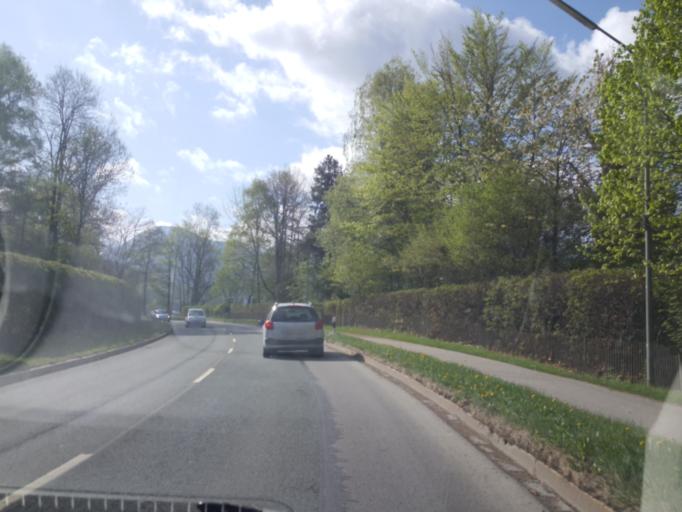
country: DE
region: Bavaria
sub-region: Upper Bavaria
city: Tegernsee
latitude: 47.7261
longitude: 11.7440
